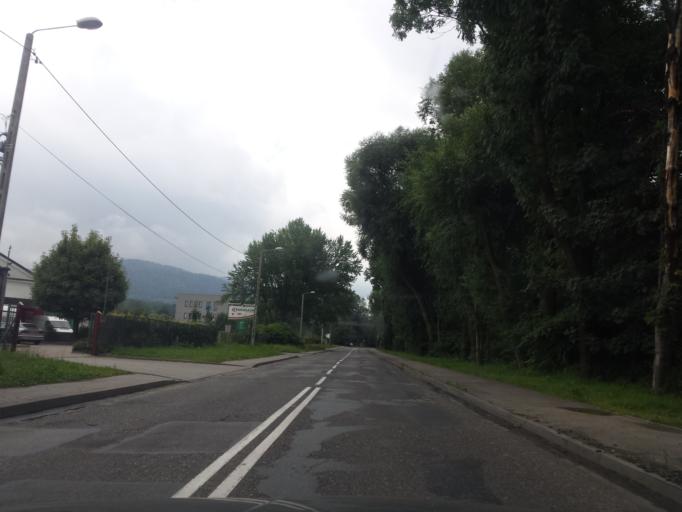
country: PL
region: Silesian Voivodeship
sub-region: Bielsko-Biala
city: Bielsko-Biala
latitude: 49.7964
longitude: 19.0560
